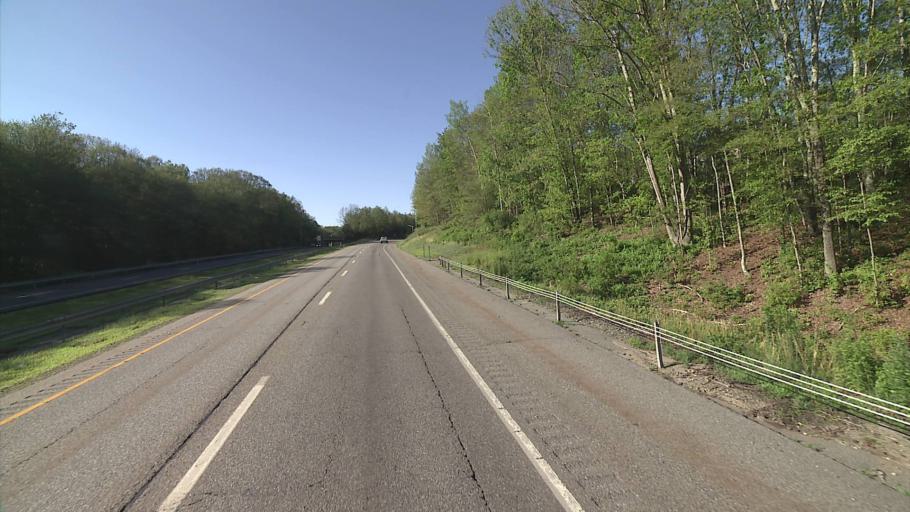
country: US
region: Connecticut
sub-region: Windham County
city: Danielson
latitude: 41.7677
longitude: -71.8723
